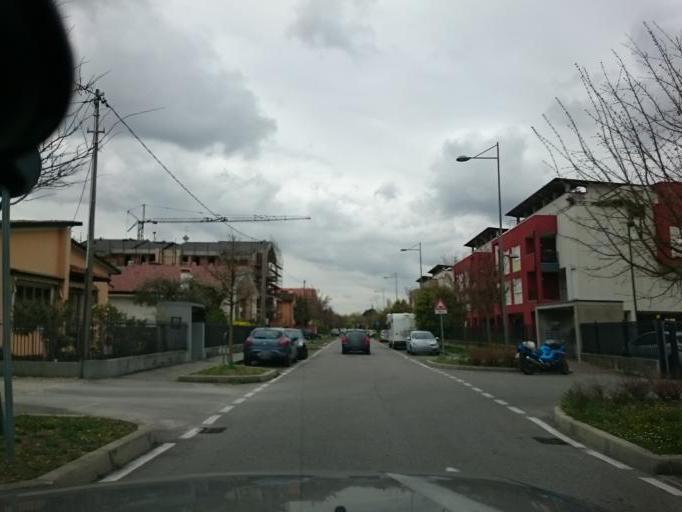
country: IT
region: Veneto
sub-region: Provincia di Padova
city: Padova
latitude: 45.3893
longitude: 11.9063
